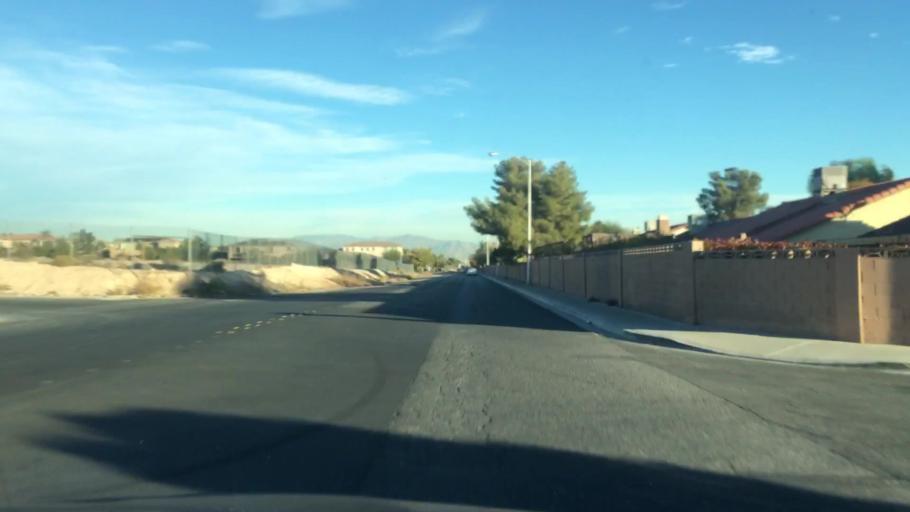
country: US
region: Nevada
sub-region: Clark County
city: Paradise
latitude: 36.0440
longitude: -115.1498
